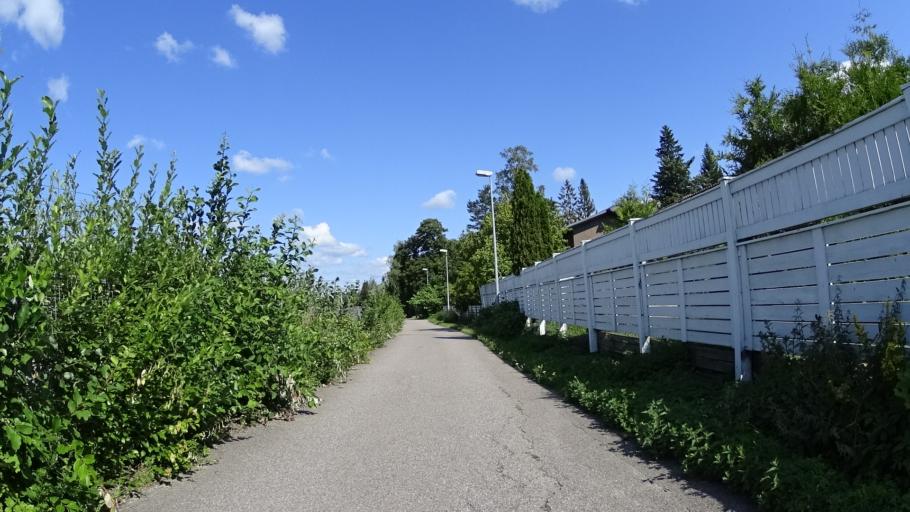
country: FI
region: Uusimaa
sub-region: Helsinki
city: Jaervenpaeae
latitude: 60.4659
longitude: 25.0995
